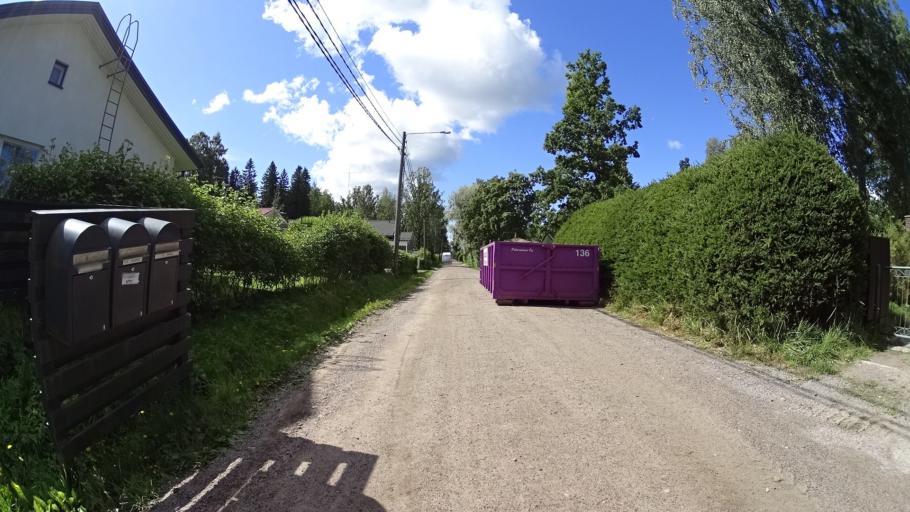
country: FI
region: Uusimaa
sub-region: Helsinki
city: Kauniainen
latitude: 60.2389
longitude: 24.7513
